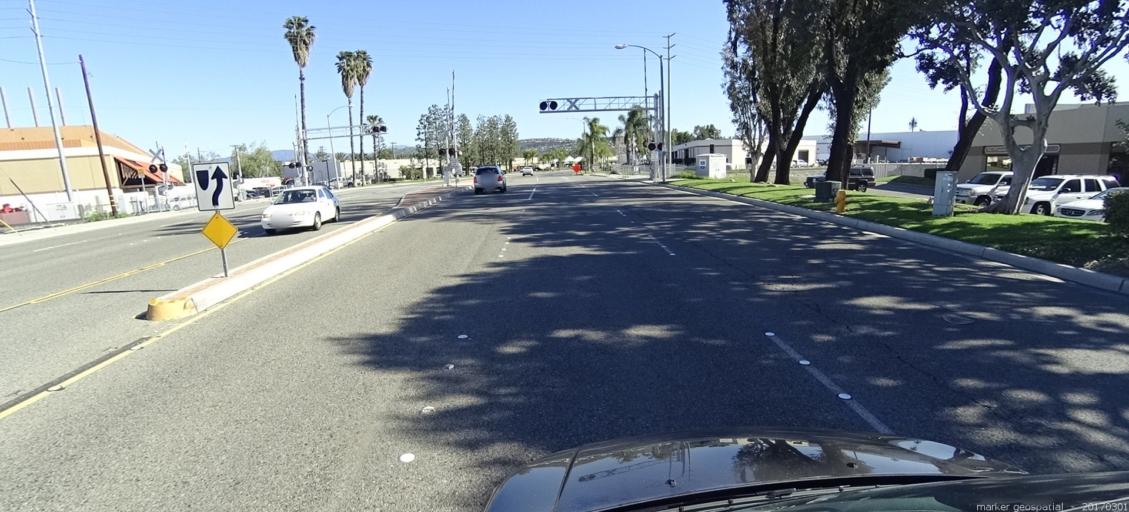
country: US
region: California
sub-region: Orange County
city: Placentia
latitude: 33.8597
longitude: -117.8396
